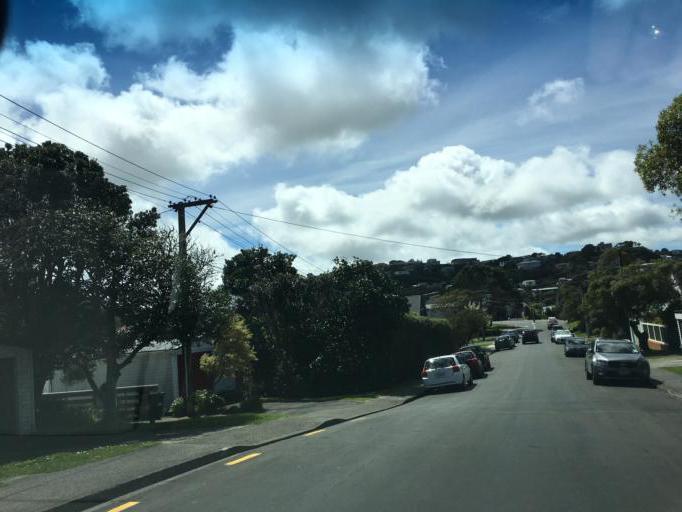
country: NZ
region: Wellington
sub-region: Wellington City
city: Wellington
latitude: -41.2467
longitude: 174.7949
